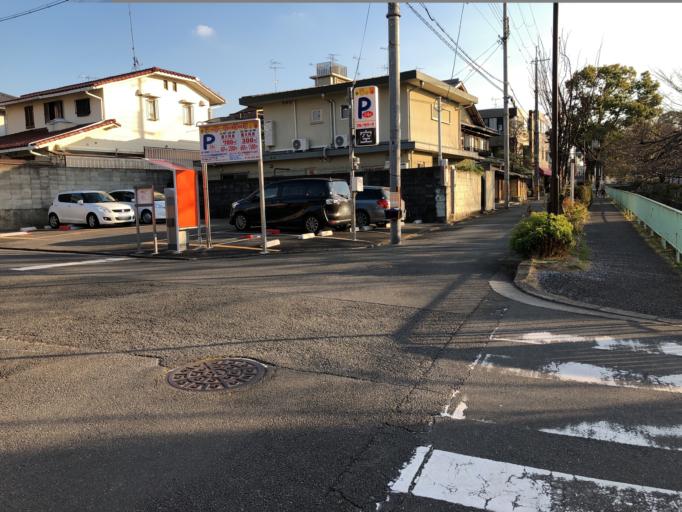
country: JP
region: Kyoto
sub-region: Kyoto-shi
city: Kamigyo-ku
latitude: 35.0340
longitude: 135.7888
